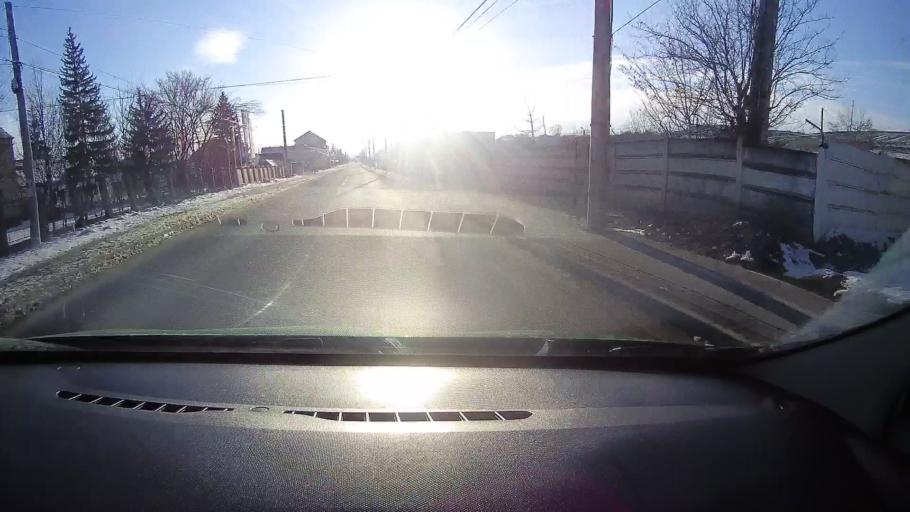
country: RO
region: Sibiu
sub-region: Oras Agnita
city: Ruja
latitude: 45.9826
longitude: 24.6424
